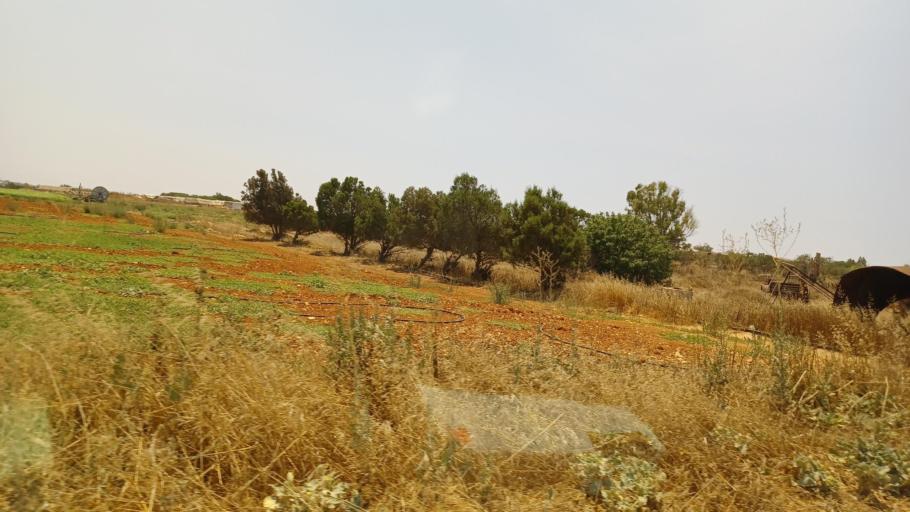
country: CY
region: Ammochostos
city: Liopetri
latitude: 34.9665
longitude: 33.8498
